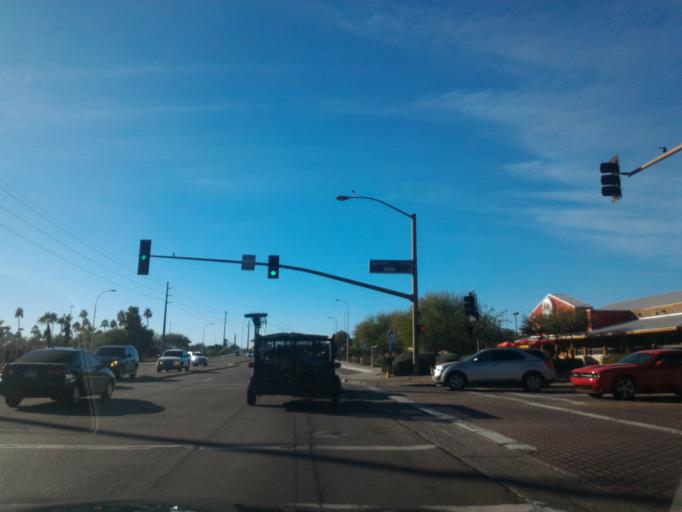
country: US
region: Arizona
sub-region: Maricopa County
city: Guadalupe
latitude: 33.3054
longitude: -111.9670
